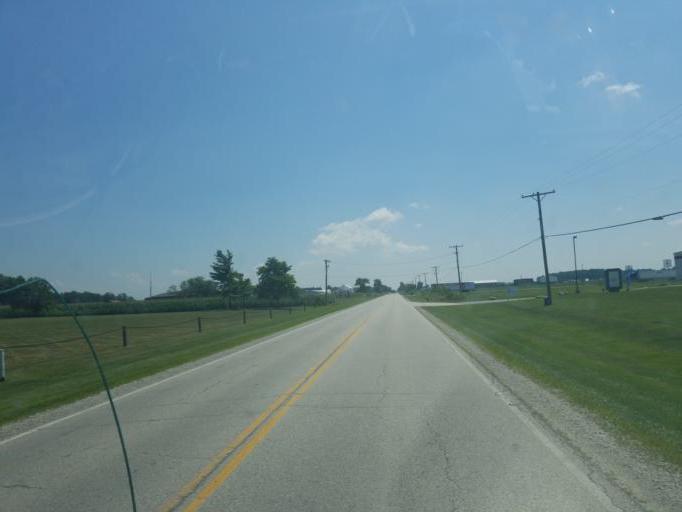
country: US
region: Ohio
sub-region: Shelby County
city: Botkins
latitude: 40.4337
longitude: -84.1779
